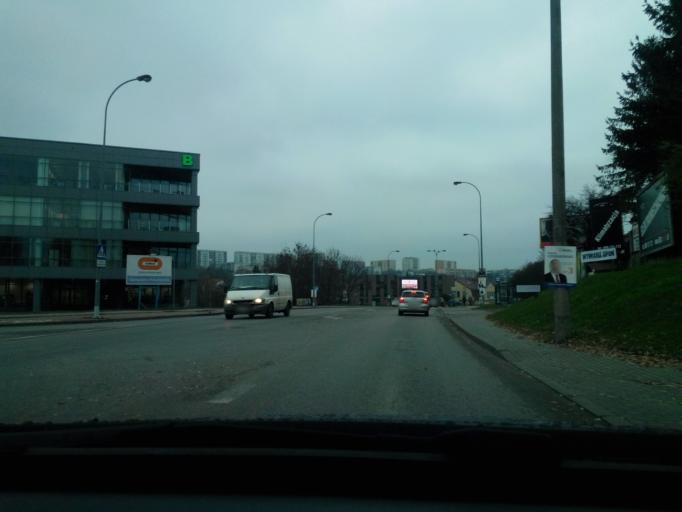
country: PL
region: Pomeranian Voivodeship
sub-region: Gdansk
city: Gdansk
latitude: 54.3539
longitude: 18.5958
